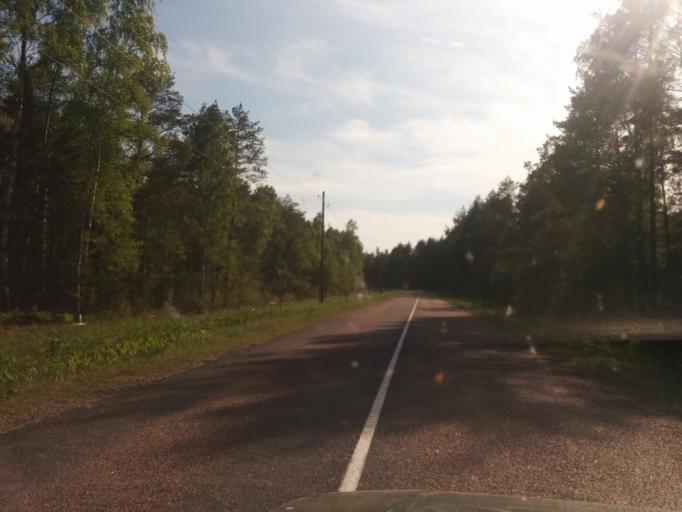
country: LV
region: Dundaga
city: Dundaga
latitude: 57.6547
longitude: 22.2725
